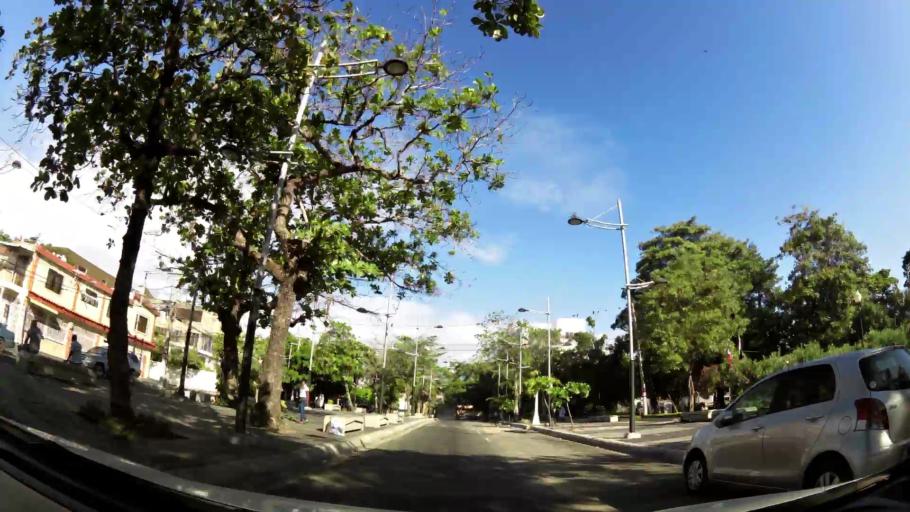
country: DO
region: Nacional
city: Ciudad Nueva
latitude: 18.4656
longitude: -69.8948
